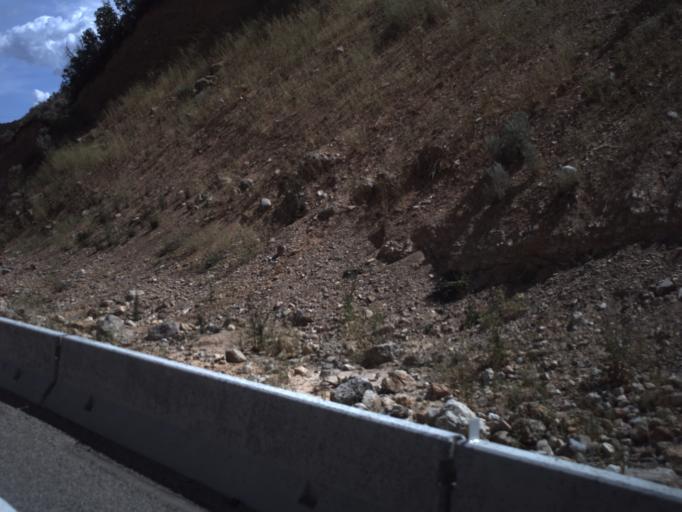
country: US
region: Utah
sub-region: Utah County
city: Woodland Hills
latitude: 39.9720
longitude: -111.5075
